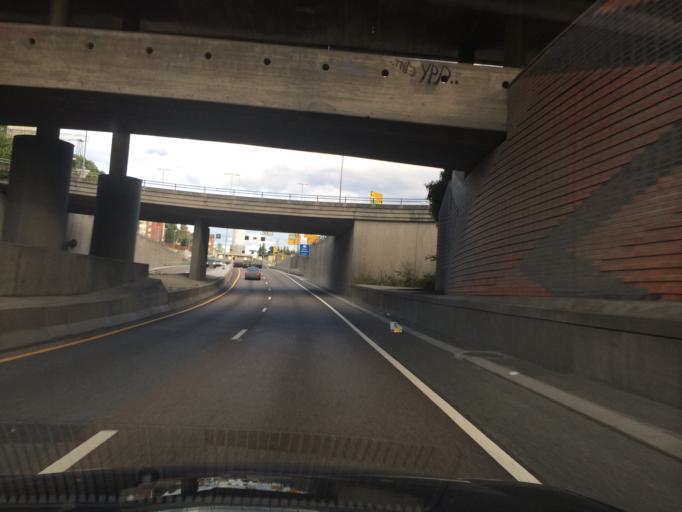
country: NO
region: Oslo
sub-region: Oslo
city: Oslo
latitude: 59.9376
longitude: 10.7844
